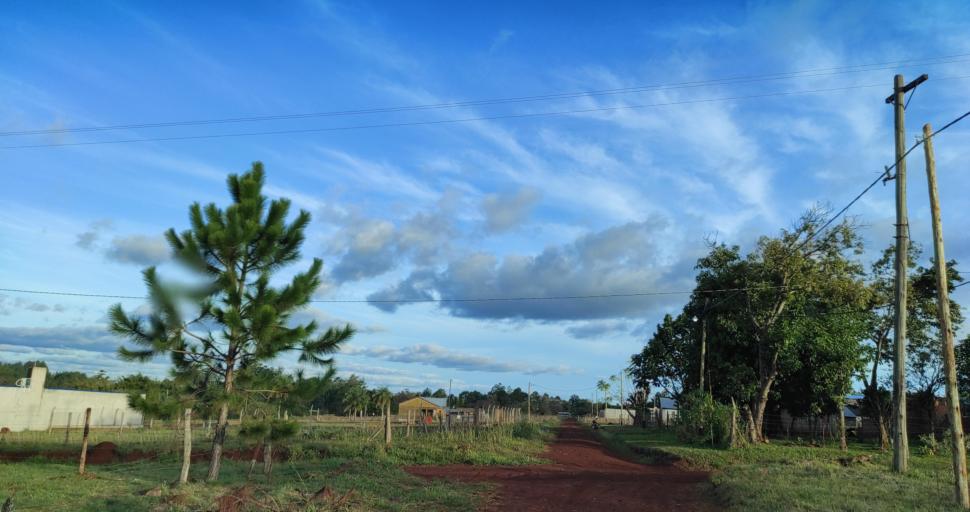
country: AR
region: Misiones
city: Garupa
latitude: -27.5228
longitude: -55.8536
